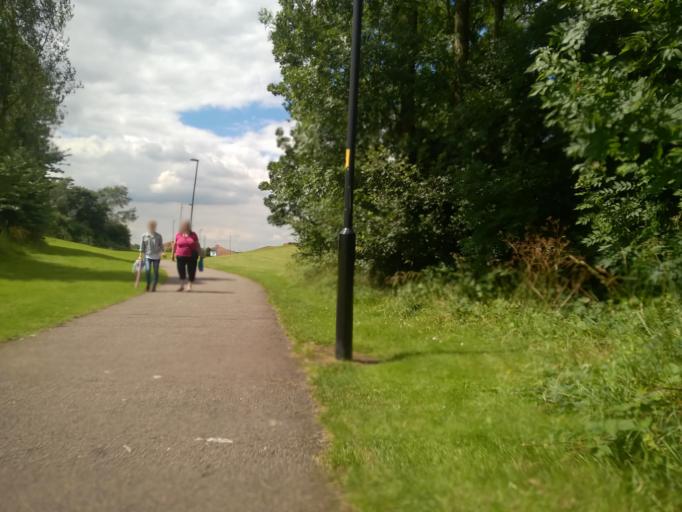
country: GB
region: England
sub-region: Leicestershire
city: Anstey
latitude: 52.6660
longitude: -1.1609
